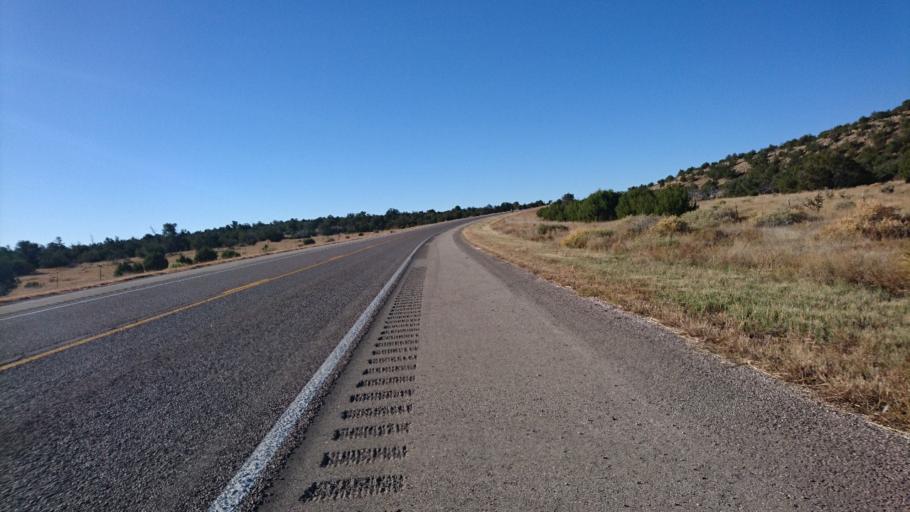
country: US
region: New Mexico
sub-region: Cibola County
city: Grants
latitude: 34.9668
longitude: -107.9129
